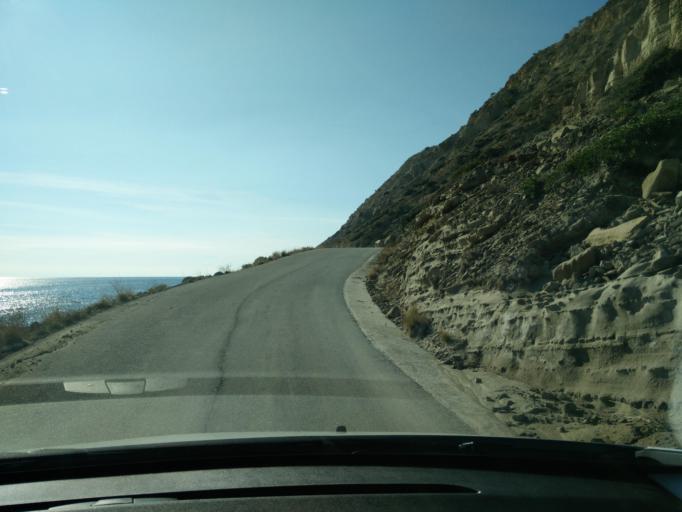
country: GR
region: Crete
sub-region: Nomos Lasithiou
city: Gra Liyia
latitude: 34.9925
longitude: 25.5528
